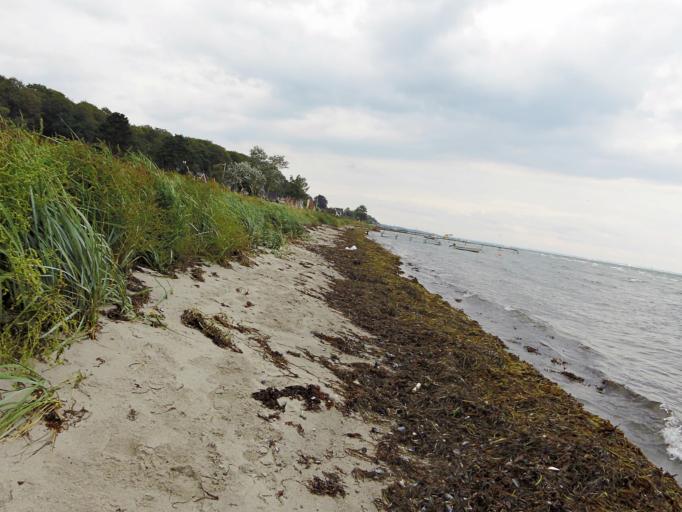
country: DK
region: Capital Region
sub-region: Fredensborg Kommune
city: Humlebaek
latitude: 55.9429
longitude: 12.5273
